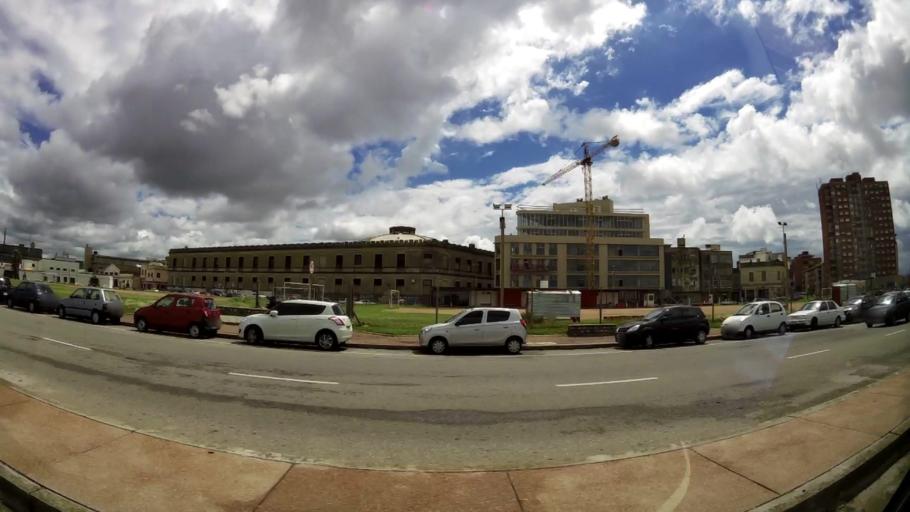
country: UY
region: Montevideo
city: Montevideo
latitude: -34.9120
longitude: -56.2121
